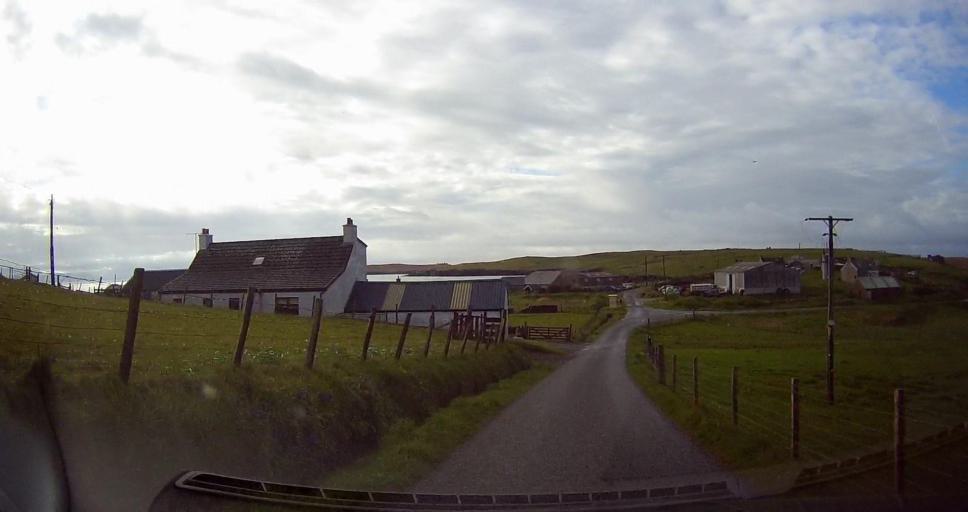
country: GB
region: Scotland
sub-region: Shetland Islands
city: Sandwick
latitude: 60.0510
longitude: -1.2067
